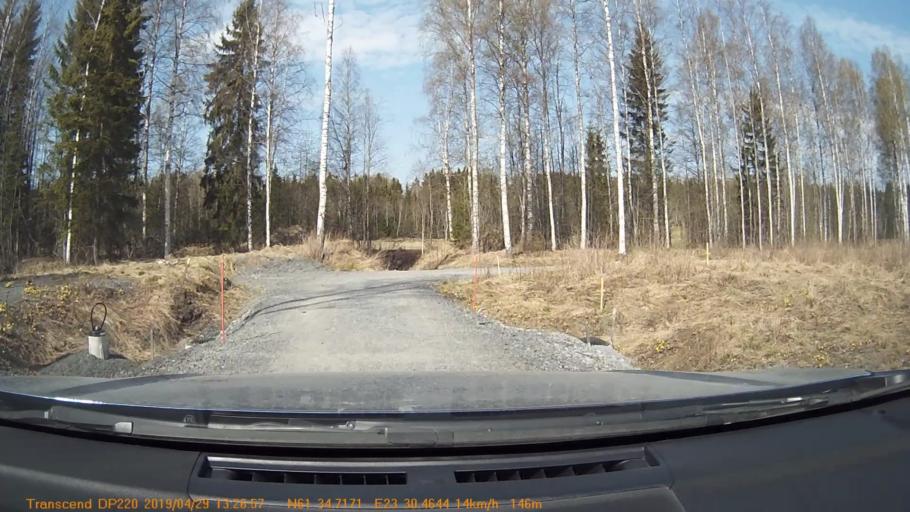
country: FI
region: Pirkanmaa
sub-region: Tampere
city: Yloejaervi
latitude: 61.5785
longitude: 23.5078
